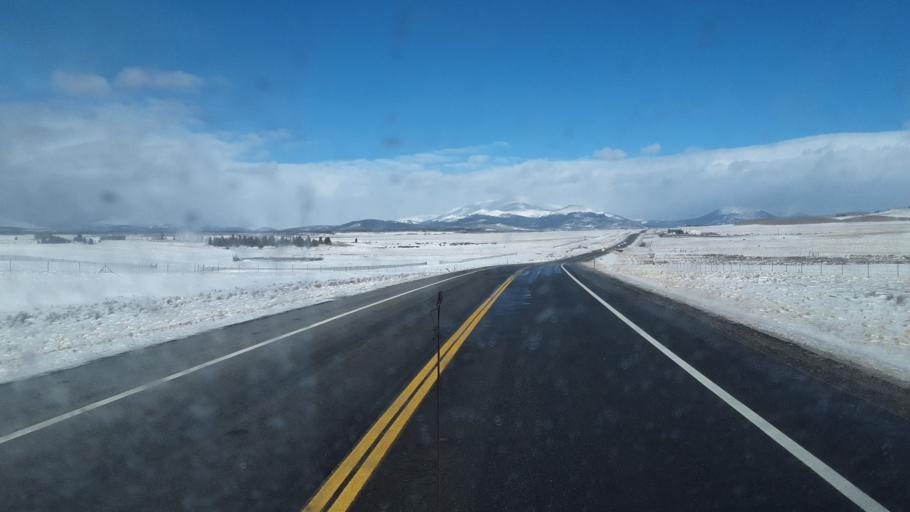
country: US
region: Colorado
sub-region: Park County
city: Fairplay
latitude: 39.1689
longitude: -106.0018
